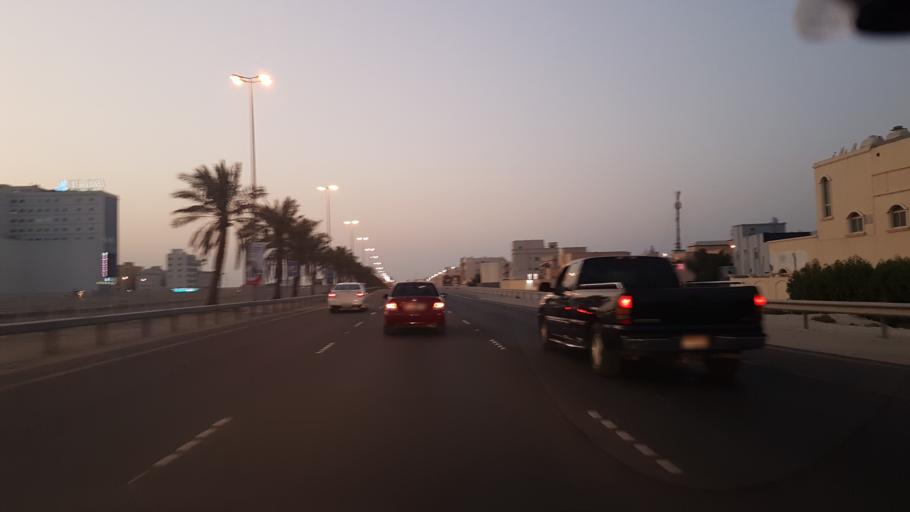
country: BH
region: Northern
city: Ar Rifa'
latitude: 26.1532
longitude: 50.5721
